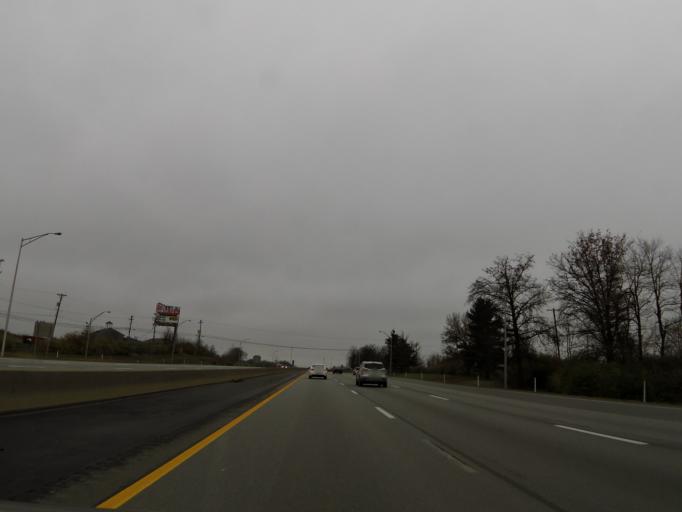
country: US
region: Kentucky
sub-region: Scott County
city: Georgetown
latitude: 38.2219
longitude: -84.5371
